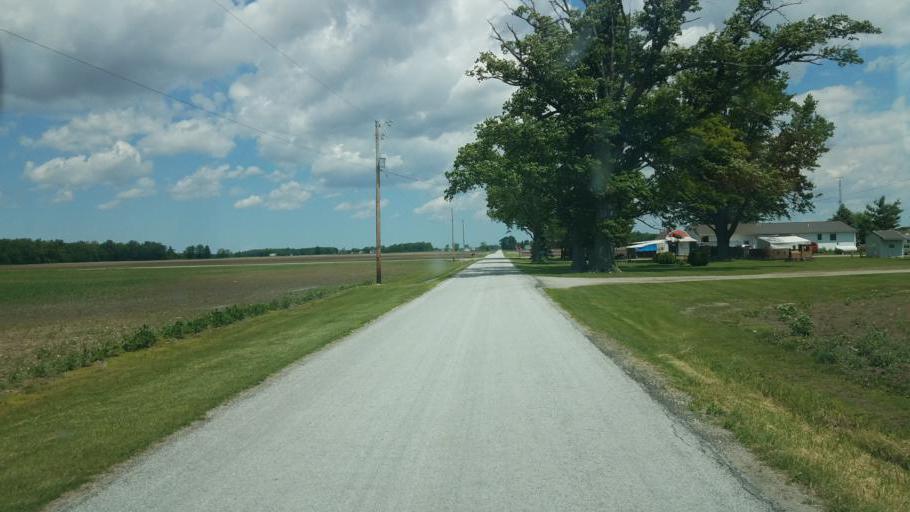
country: US
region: Ohio
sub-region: Hardin County
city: Kenton
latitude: 40.6709
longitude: -83.4776
